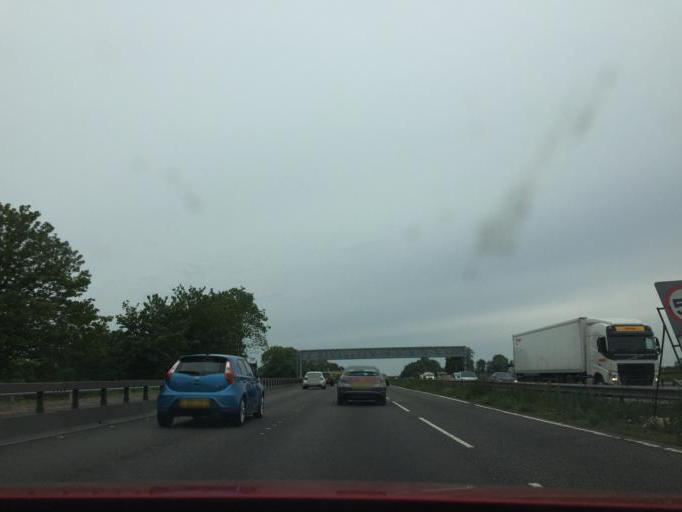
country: GB
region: England
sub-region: Solihull
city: Meriden
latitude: 52.4673
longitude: -1.6116
